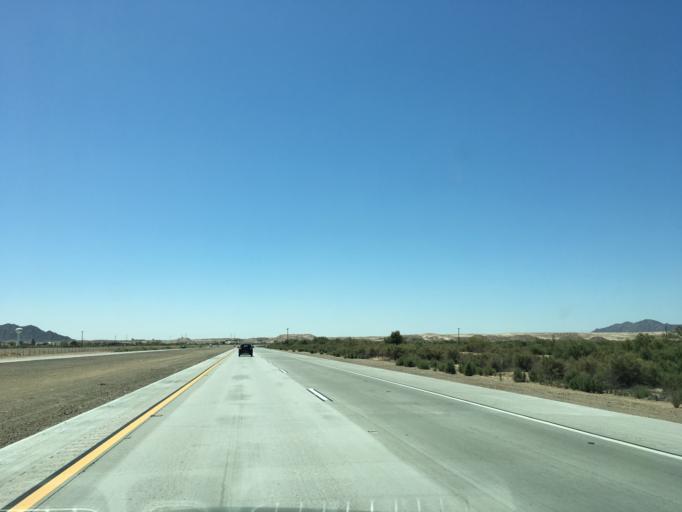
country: US
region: Arizona
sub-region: Yuma County
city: Yuma
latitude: 32.7403
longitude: -114.6766
